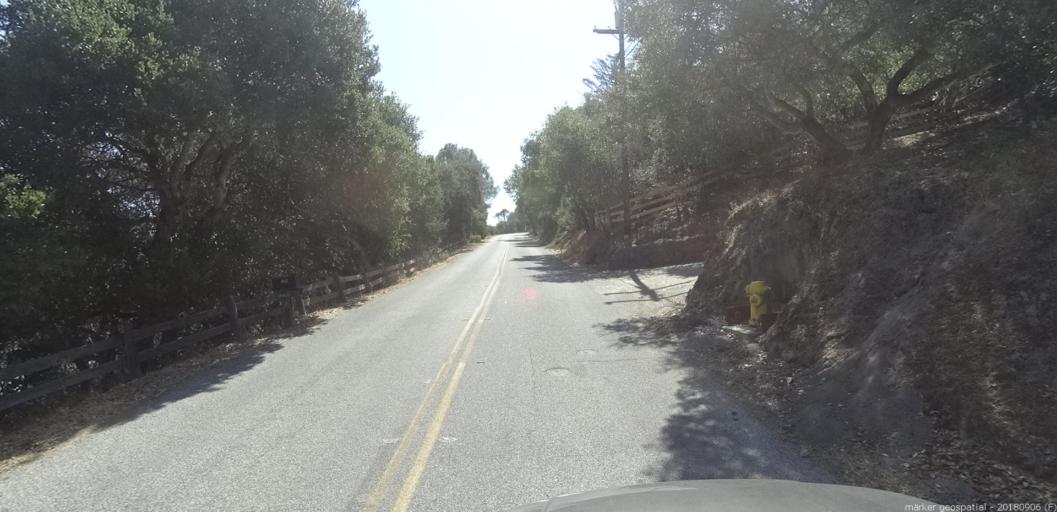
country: US
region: California
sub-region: Monterey County
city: Salinas
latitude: 36.5778
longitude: -121.6301
